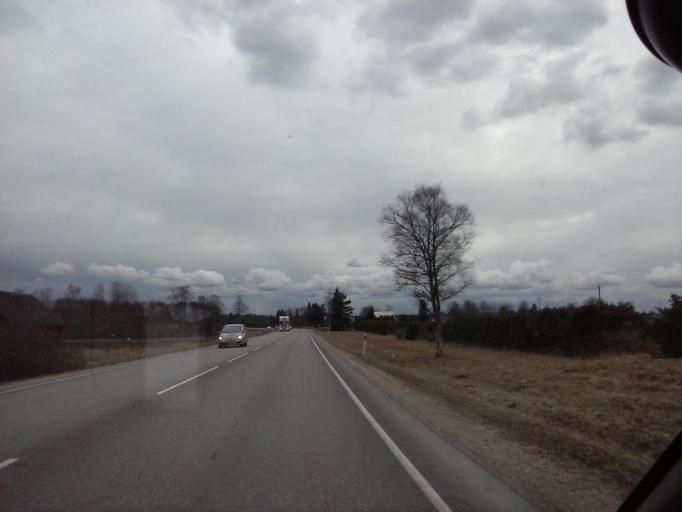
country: EE
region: Harju
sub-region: Anija vald
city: Kehra
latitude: 59.1194
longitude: 25.3152
